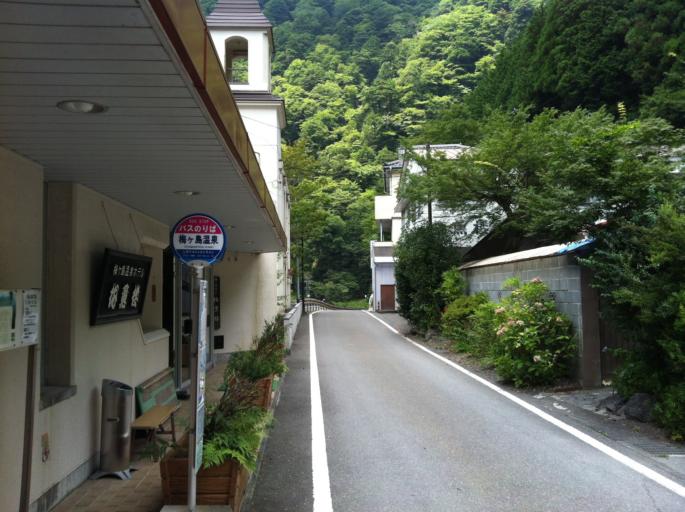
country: JP
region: Shizuoka
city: Fujinomiya
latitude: 35.3053
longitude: 138.3393
